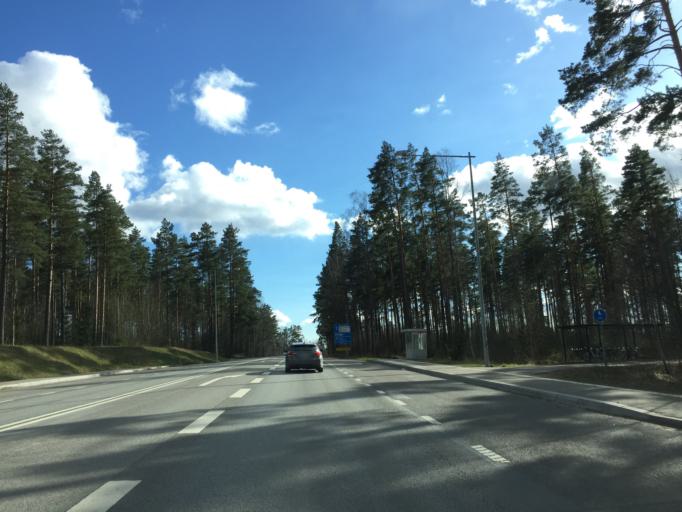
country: SE
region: OErebro
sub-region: Kumla Kommun
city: Kumla
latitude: 59.1461
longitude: 15.1395
